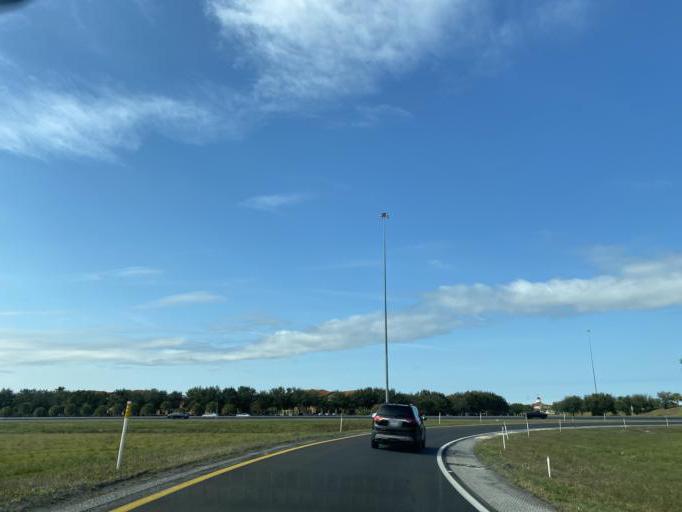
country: US
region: Florida
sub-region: Seminole County
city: Heathrow
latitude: 28.7543
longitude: -81.3625
